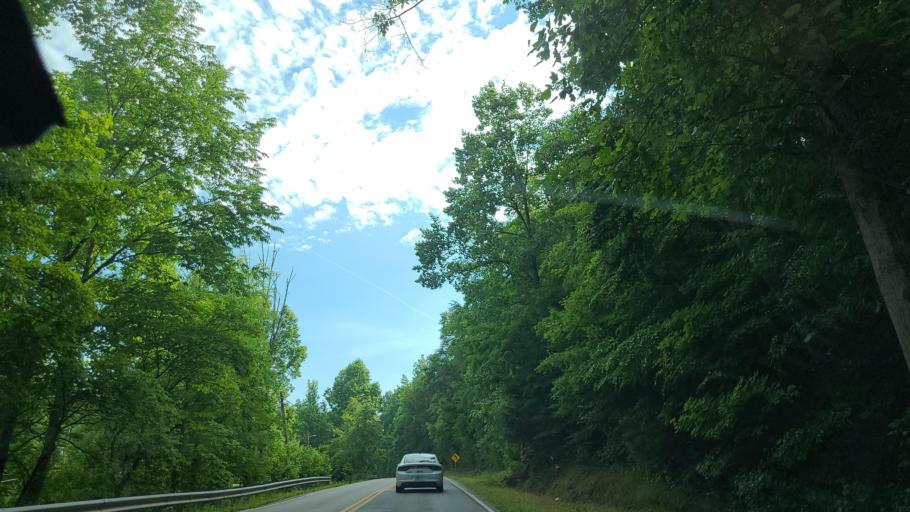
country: US
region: Kentucky
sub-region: Whitley County
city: Williamsburg
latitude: 36.7437
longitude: -84.0633
